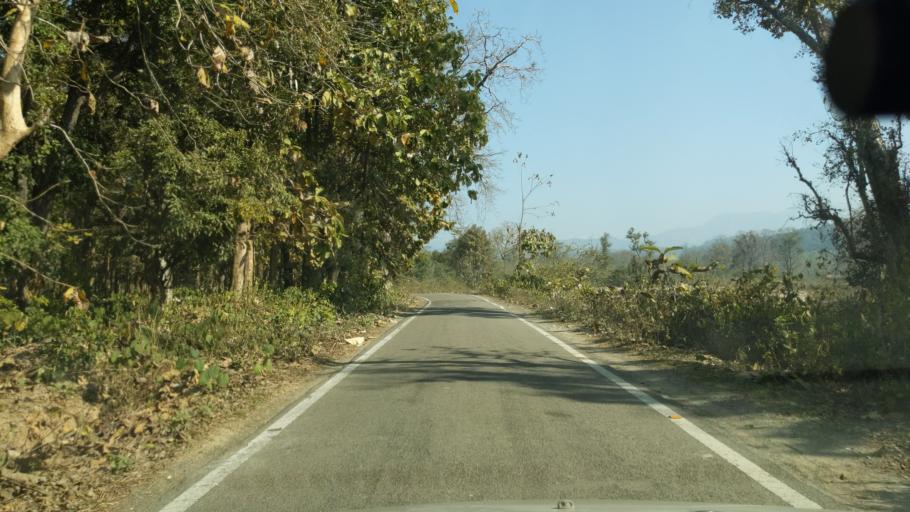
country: IN
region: Uttarakhand
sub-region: Naini Tal
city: Ramnagar
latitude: 29.4172
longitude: 79.1372
